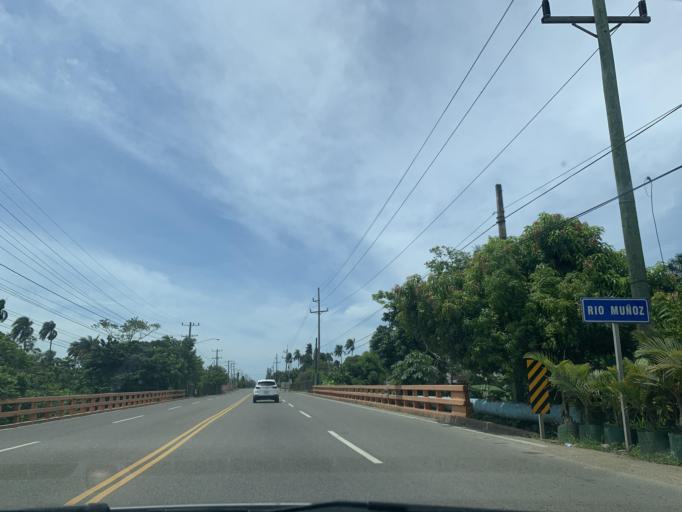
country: DO
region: Puerto Plata
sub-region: Puerto Plata
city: Puerto Plata
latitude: 19.7549
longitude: -70.6428
